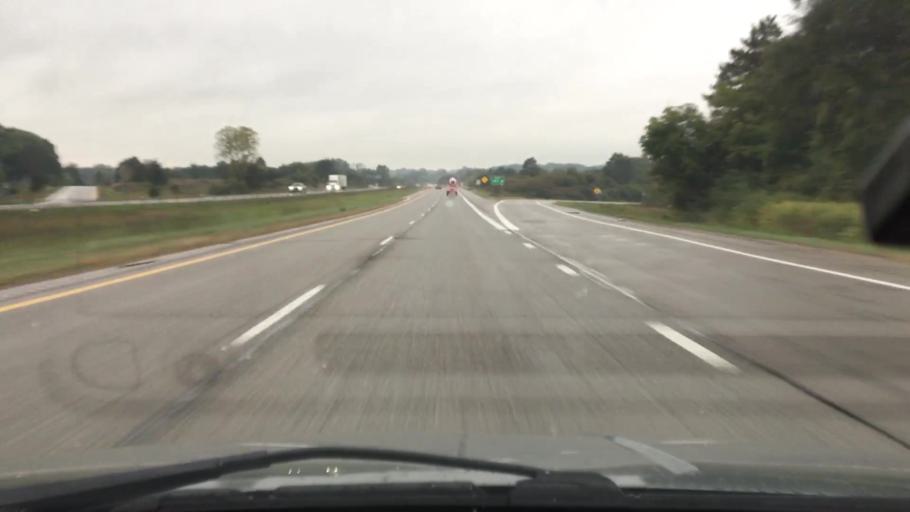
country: US
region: Michigan
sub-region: Washtenaw County
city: Chelsea
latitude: 42.2928
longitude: -84.0647
